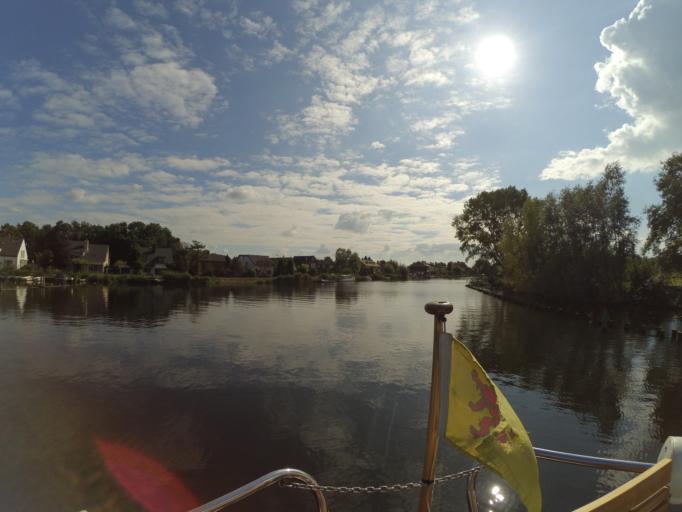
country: NL
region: Utrecht
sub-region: Stichtse Vecht
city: Vreeland
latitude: 52.2560
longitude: 5.0428
